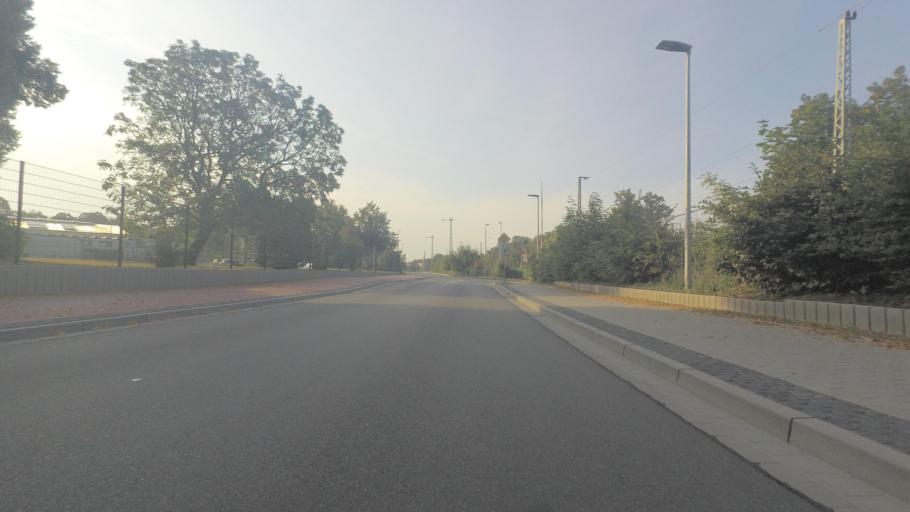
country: DE
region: Mecklenburg-Vorpommern
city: Demmin
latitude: 53.9049
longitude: 13.0485
